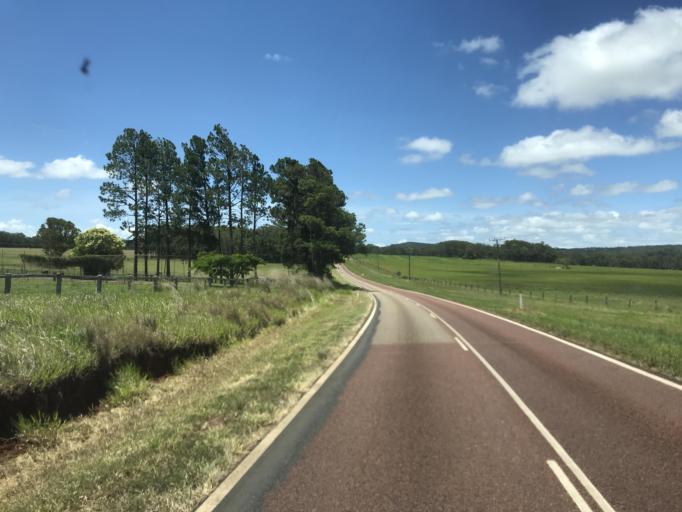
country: AU
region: Queensland
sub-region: Tablelands
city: Ravenshoe
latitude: -17.5278
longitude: 145.4540
